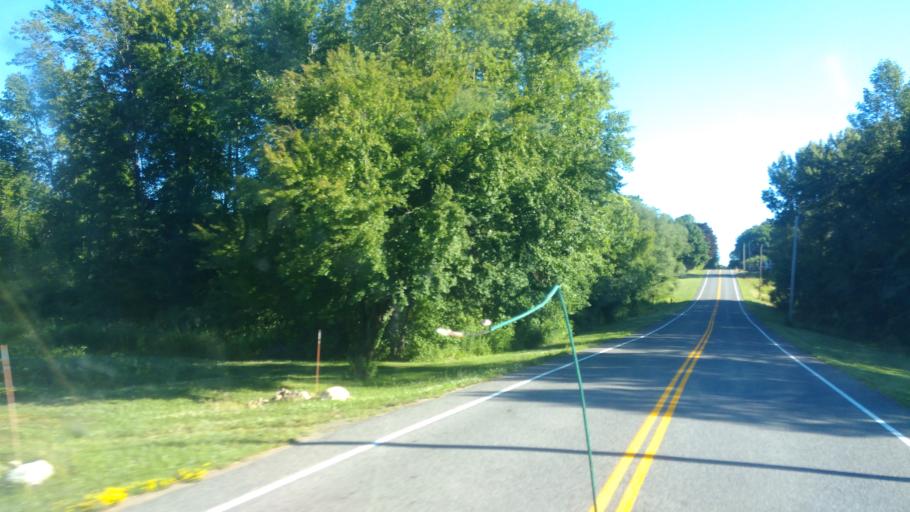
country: US
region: New York
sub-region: Wayne County
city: Sodus
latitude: 43.2169
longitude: -77.1109
